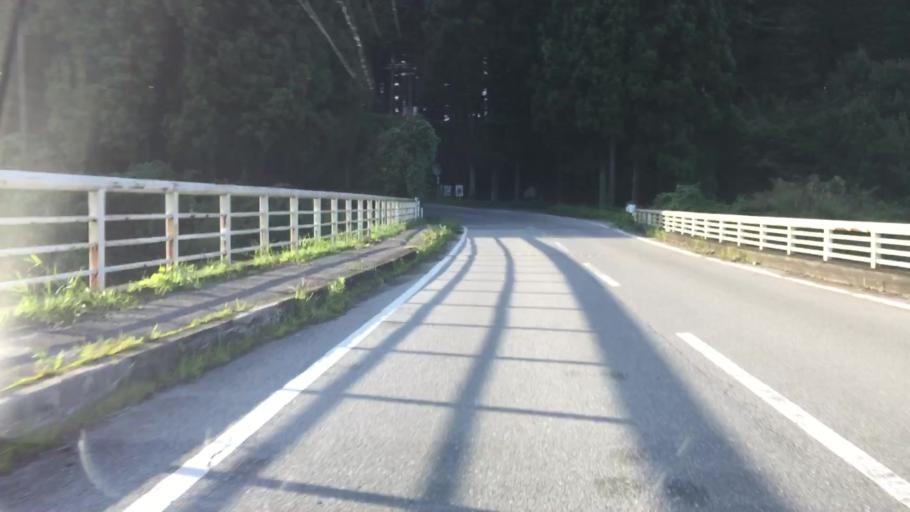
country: JP
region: Tochigi
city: Imaichi
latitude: 36.7633
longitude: 139.6974
